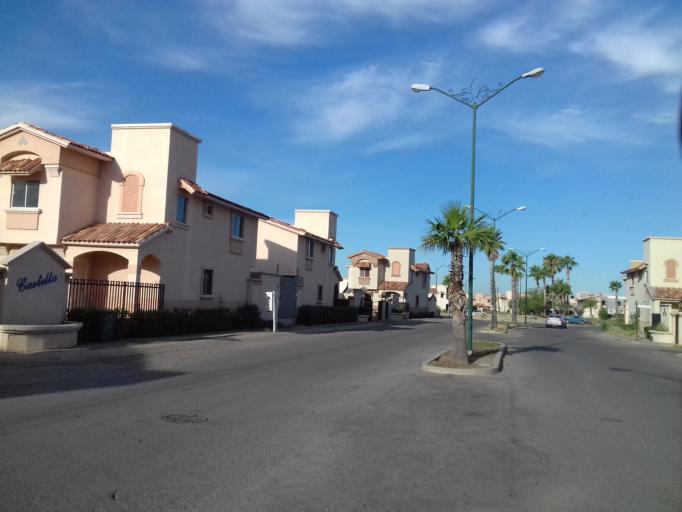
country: MX
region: Sonora
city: Hermosillo
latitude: 29.1154
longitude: -111.0355
